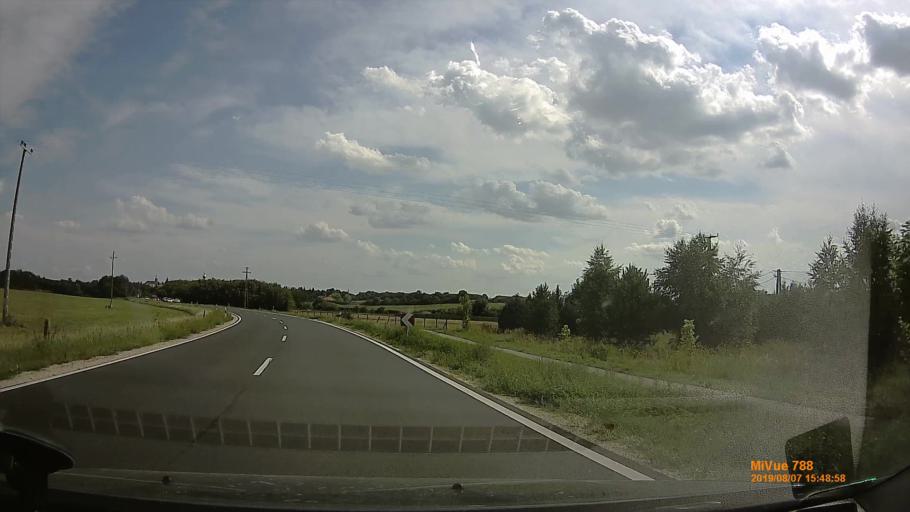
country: HU
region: Vas
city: Jak
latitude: 47.1555
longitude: 16.6382
